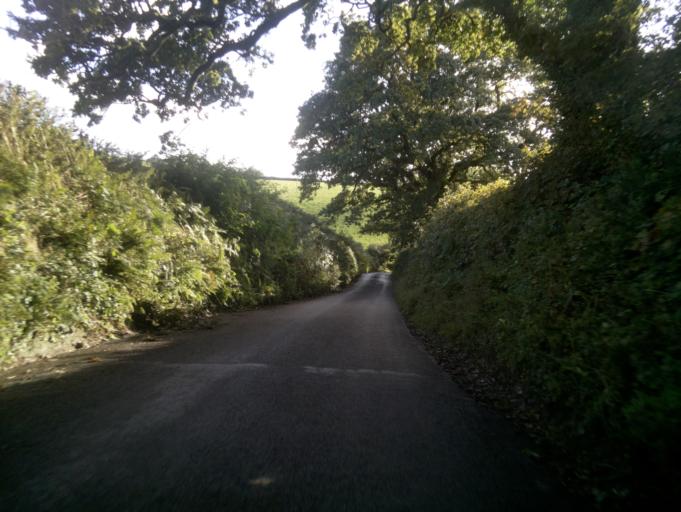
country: GB
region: England
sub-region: Devon
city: Dartmouth
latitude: 50.3493
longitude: -3.6351
